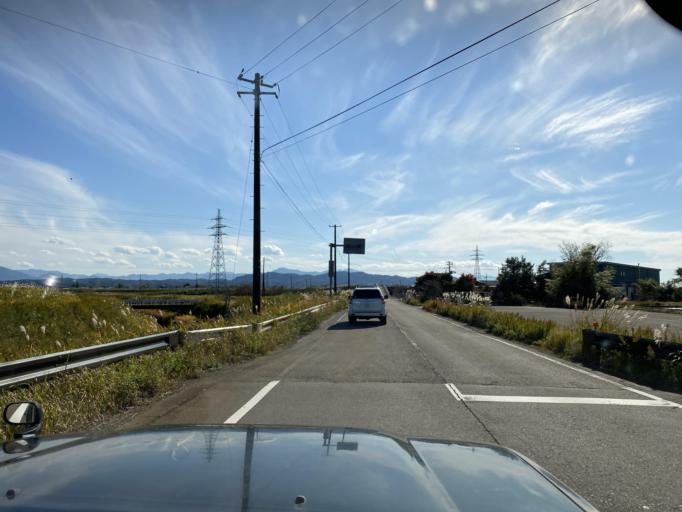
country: JP
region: Niigata
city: Niitsu-honcho
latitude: 37.7909
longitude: 139.0802
